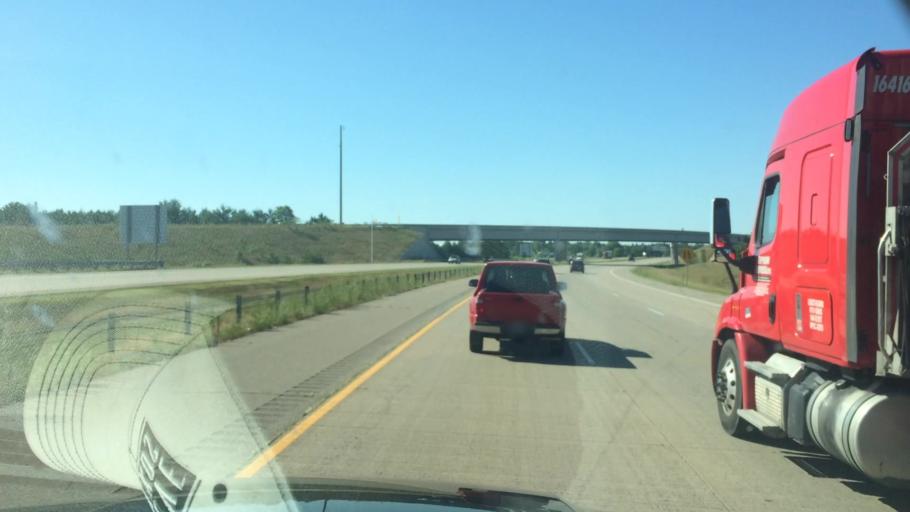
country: US
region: Wisconsin
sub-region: Marathon County
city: Rothschild
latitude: 44.8966
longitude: -89.6405
